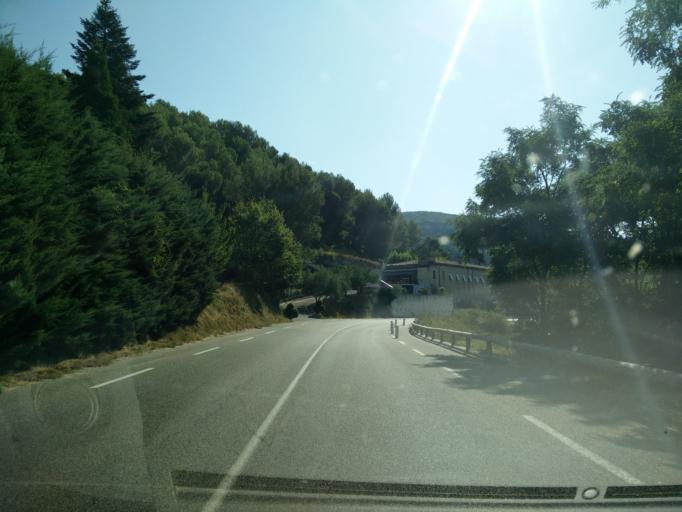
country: FR
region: Rhone-Alpes
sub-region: Departement de la Drome
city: La Begude-de-Mazenc
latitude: 44.5422
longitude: 4.9510
